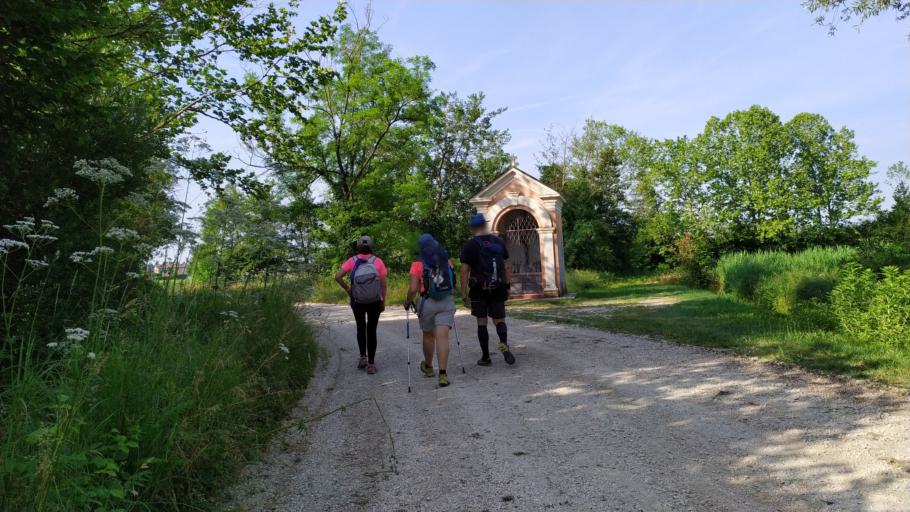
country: IT
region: Friuli Venezia Giulia
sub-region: Provincia di Pordenone
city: San Giovanni
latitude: 45.9963
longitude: 12.5013
